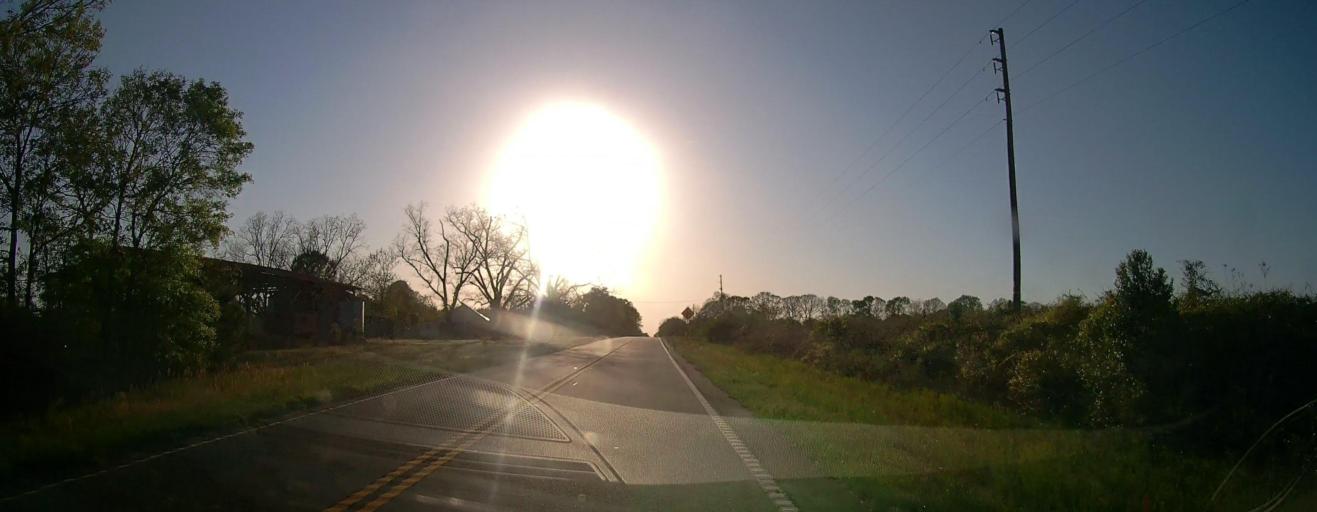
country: US
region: Georgia
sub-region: Schley County
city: Ellaville
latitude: 32.3435
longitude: -84.3600
